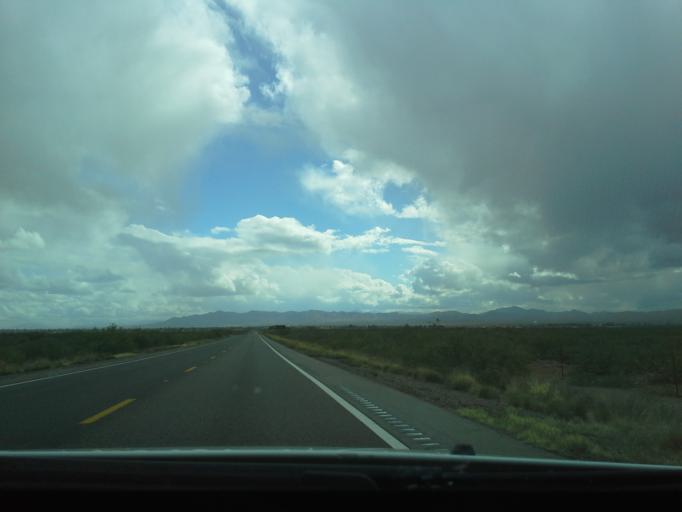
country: US
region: Arizona
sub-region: Cochise County
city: Douglas
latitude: 31.3921
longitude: -109.5107
